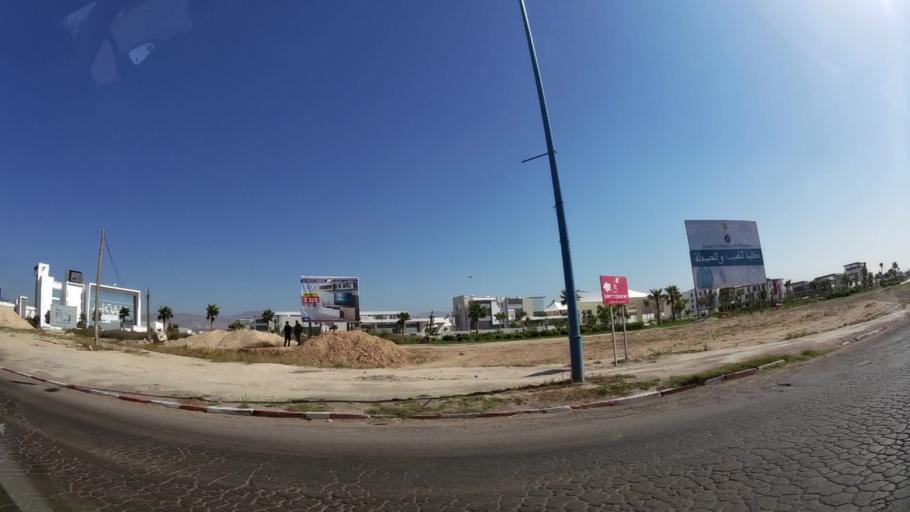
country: MA
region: Oued ed Dahab-Lagouira
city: Dakhla
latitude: 30.4049
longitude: -9.5326
